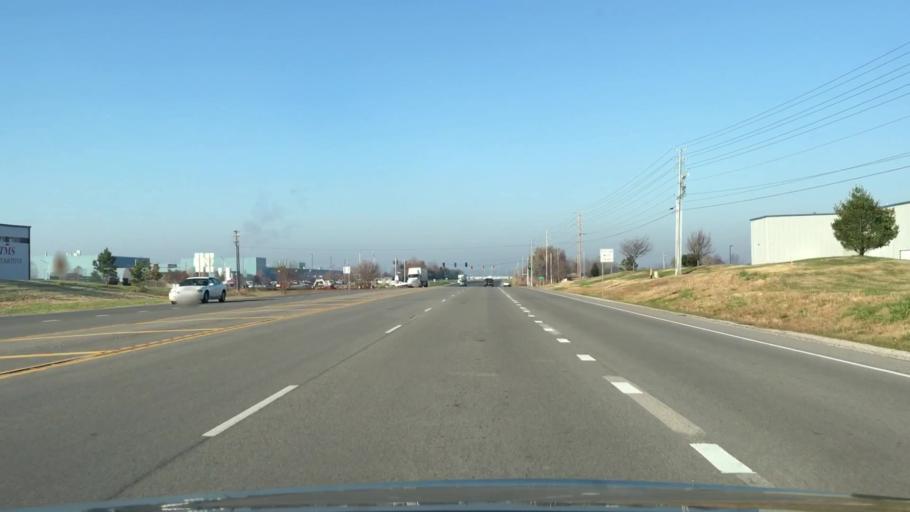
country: US
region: Kentucky
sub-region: Warren County
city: Bowling Green
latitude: 37.0331
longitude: -86.3153
